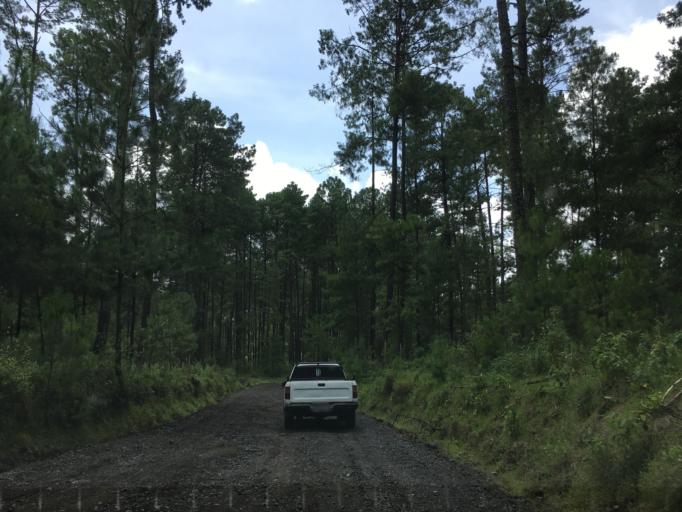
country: MX
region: Michoacan
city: Nuevo San Juan Parangaricutiro
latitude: 19.4465
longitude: -102.1831
